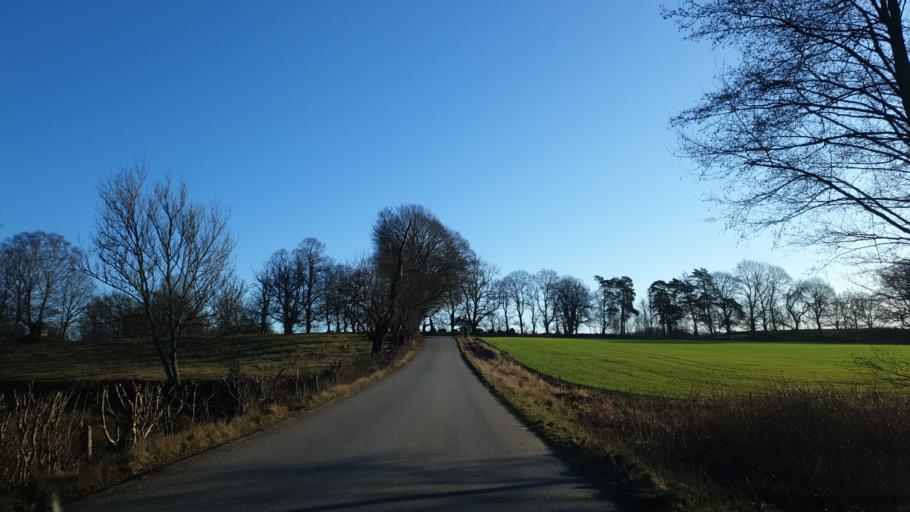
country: SE
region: Blekinge
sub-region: Karlskrona Kommun
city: Nattraby
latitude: 56.2452
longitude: 15.4199
